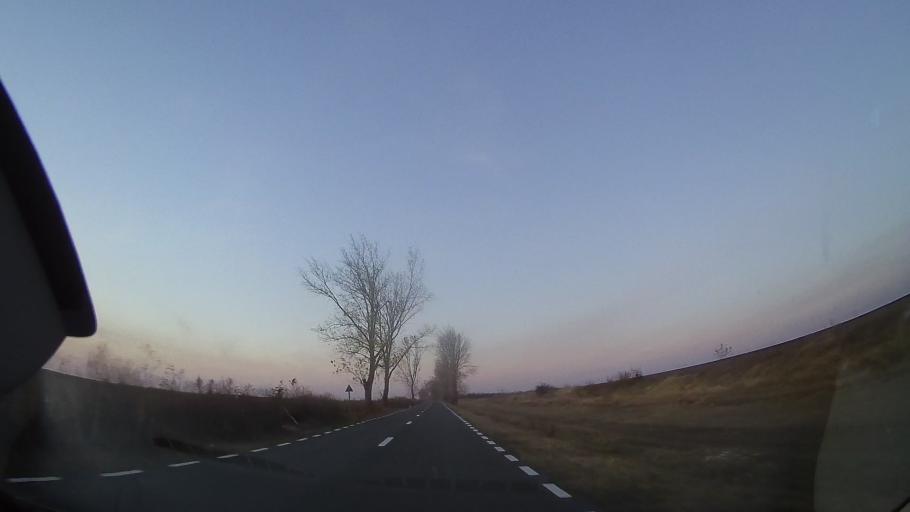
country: RO
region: Constanta
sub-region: Comuna Cobadin
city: Cobadin
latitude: 44.0404
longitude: 28.2568
